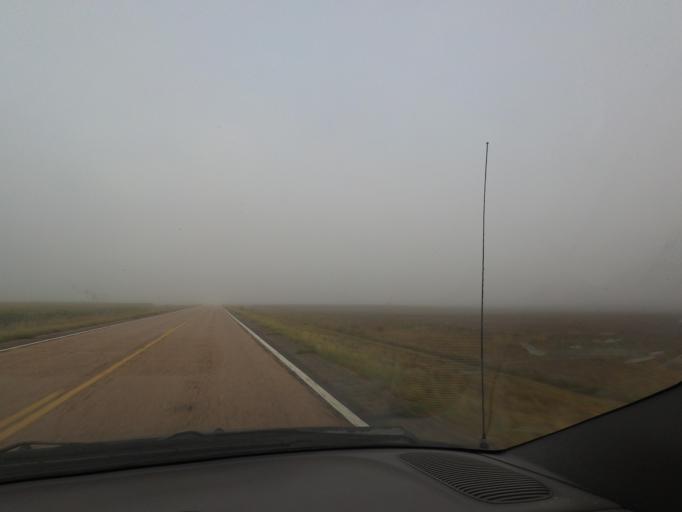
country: US
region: Colorado
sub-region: Kit Carson County
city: Burlington
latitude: 39.6565
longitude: -102.5870
